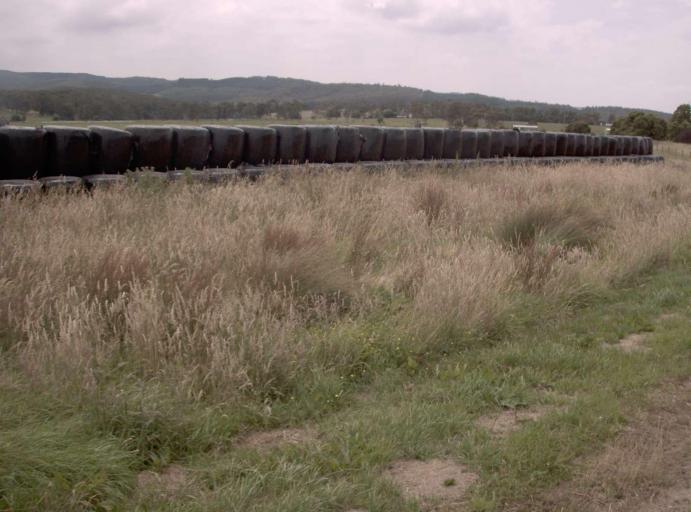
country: AU
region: Victoria
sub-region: Latrobe
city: Traralgon
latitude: -38.4974
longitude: 146.6779
